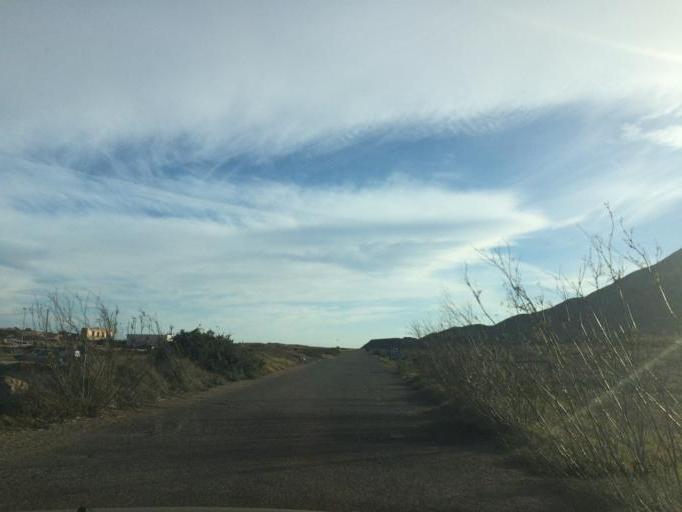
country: ES
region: Andalusia
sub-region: Provincia de Almeria
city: San Jose
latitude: 36.8033
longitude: -2.0642
